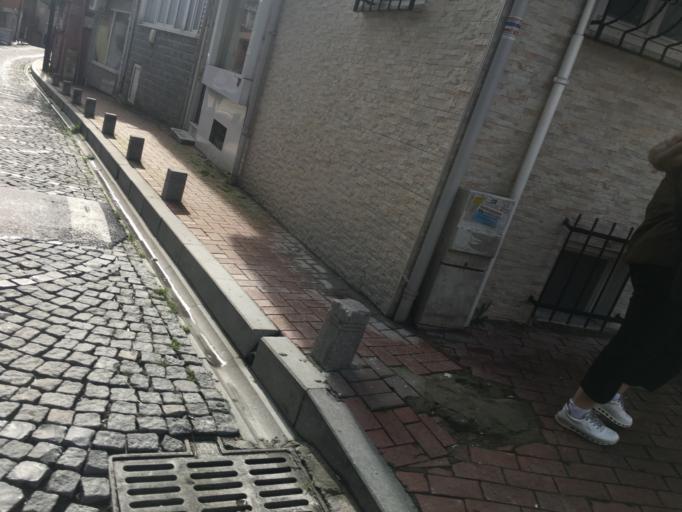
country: TR
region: Istanbul
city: UEskuedar
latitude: 41.0697
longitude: 29.0415
